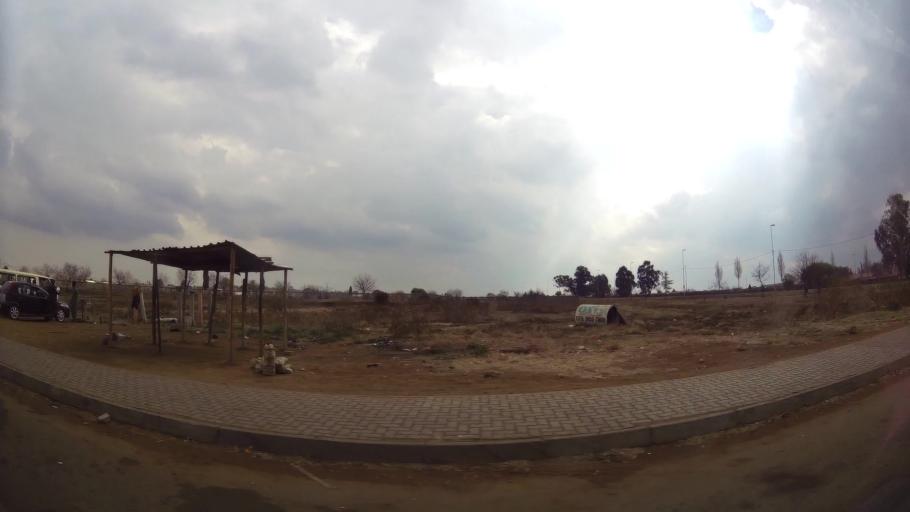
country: ZA
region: Gauteng
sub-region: Ekurhuleni Metropolitan Municipality
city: Germiston
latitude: -26.3906
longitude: 28.1607
